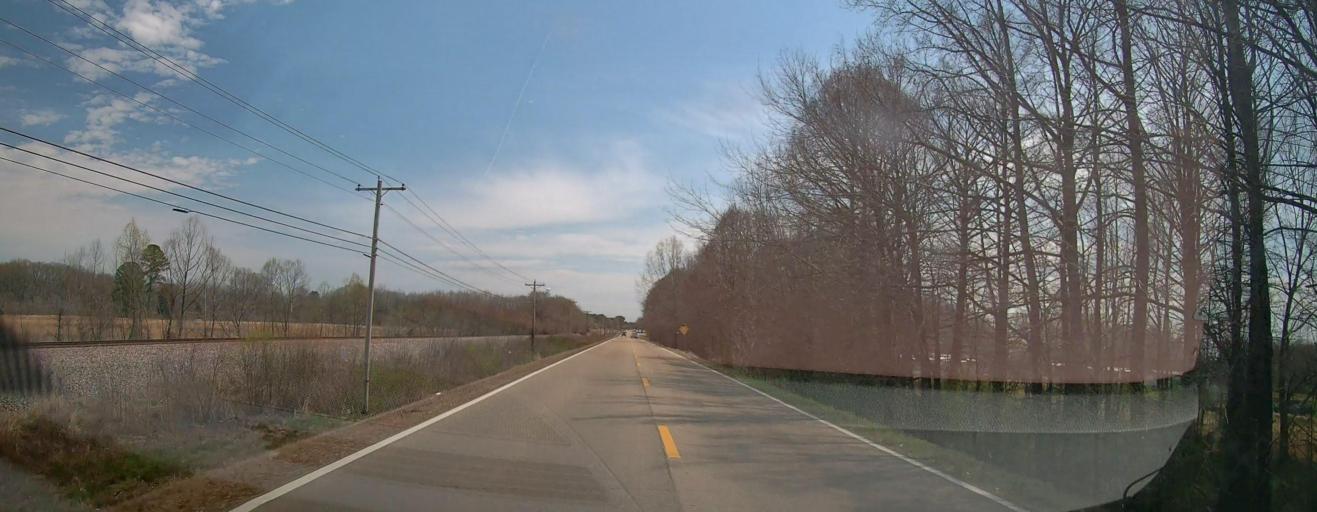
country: US
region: Mississippi
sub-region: Union County
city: New Albany
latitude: 34.5204
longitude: -89.0549
